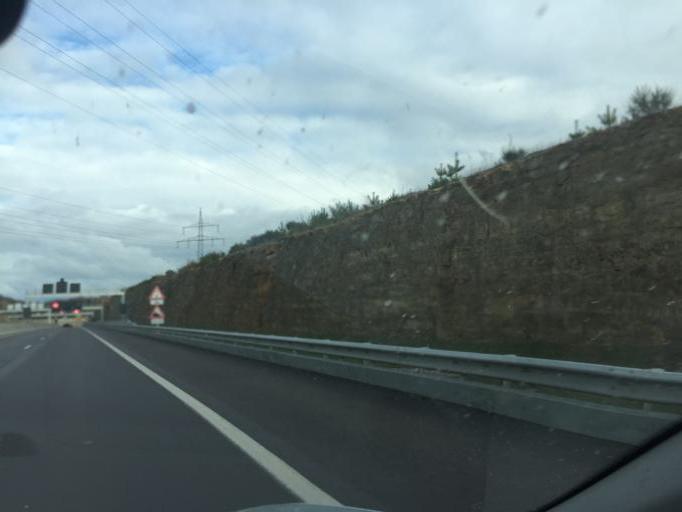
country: LU
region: Luxembourg
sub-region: Canton de Mersch
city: Lorentzweiler
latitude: 49.6836
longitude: 6.1607
